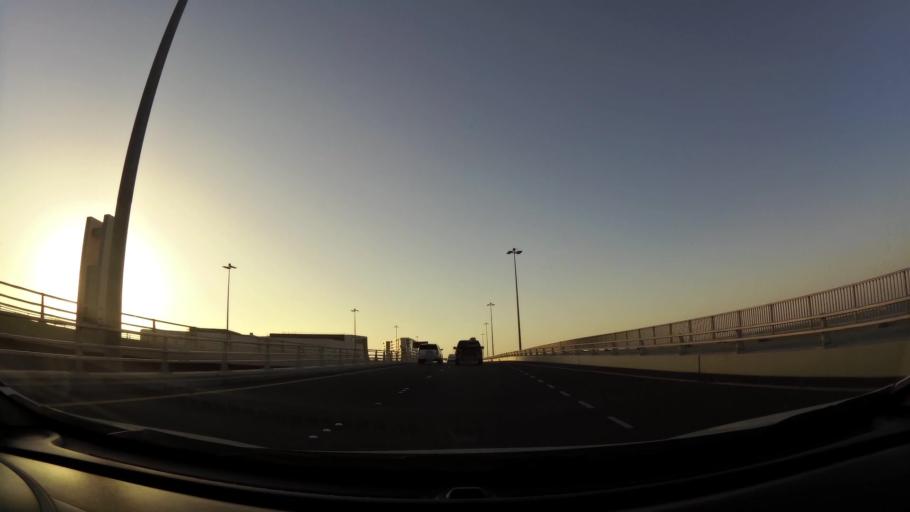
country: BH
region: Muharraq
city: Al Muharraq
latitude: 26.2481
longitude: 50.5885
